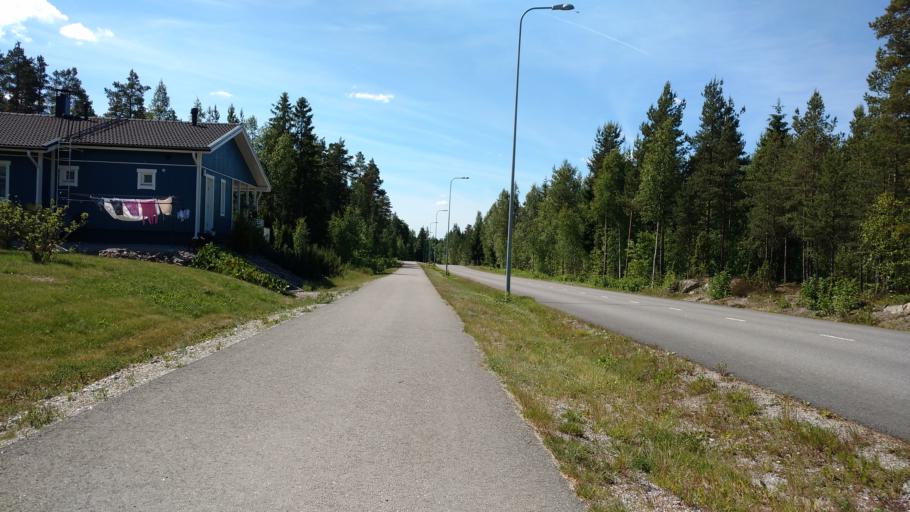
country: FI
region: Varsinais-Suomi
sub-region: Salo
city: Salo
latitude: 60.3990
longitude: 23.1887
